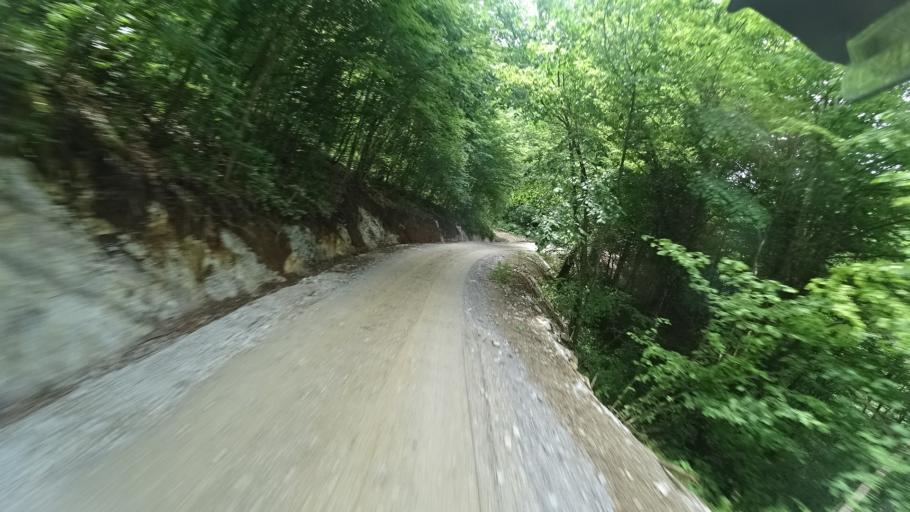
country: HR
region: Karlovacka
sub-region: Grad Karlovac
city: Slunj
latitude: 45.2142
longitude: 15.6354
